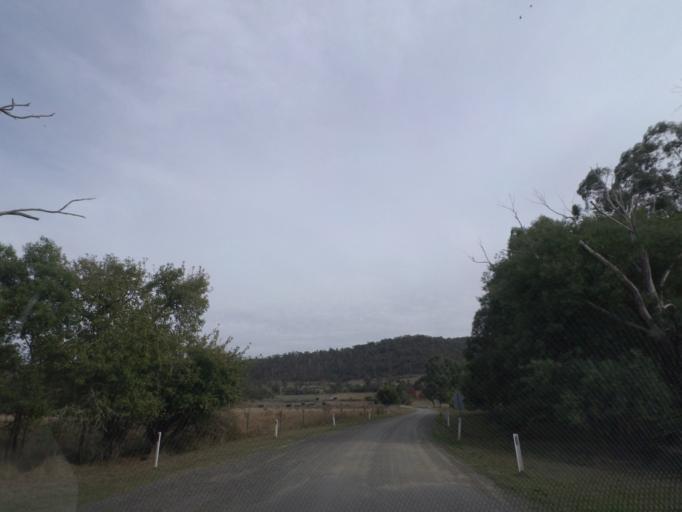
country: AU
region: Victoria
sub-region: Yarra Ranges
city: Yarra Glen
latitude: -37.5944
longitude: 145.3794
